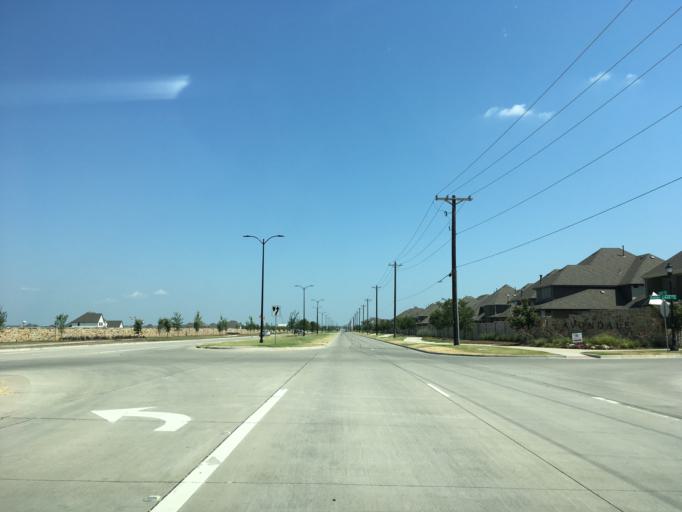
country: US
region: Texas
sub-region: Collin County
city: Prosper
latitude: 33.1924
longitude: -96.7678
